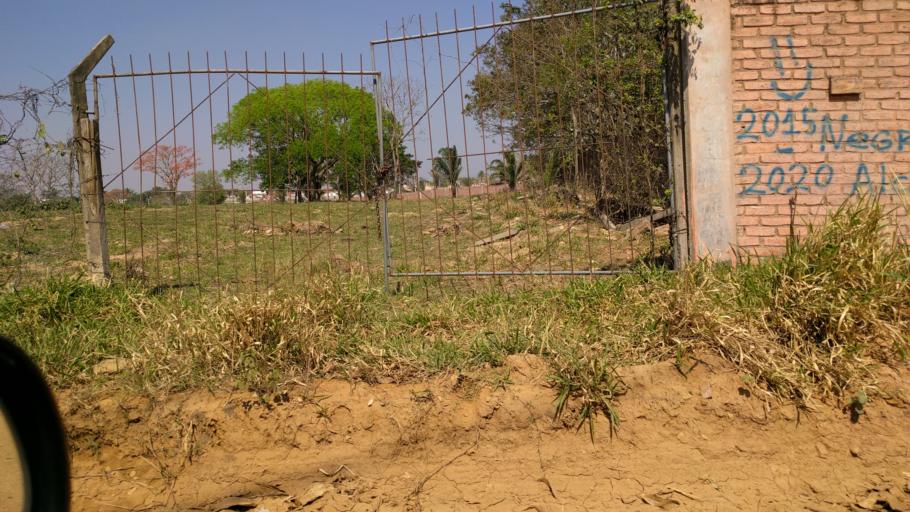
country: BO
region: Santa Cruz
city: Santa Cruz de la Sierra
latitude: -17.7558
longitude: -63.2314
